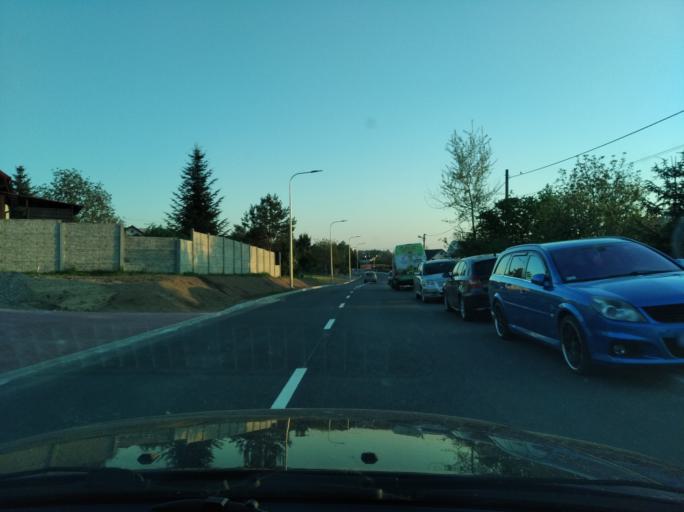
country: PL
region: Subcarpathian Voivodeship
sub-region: Powiat rzeszowski
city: Tyczyn
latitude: 50.0119
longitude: 22.0385
